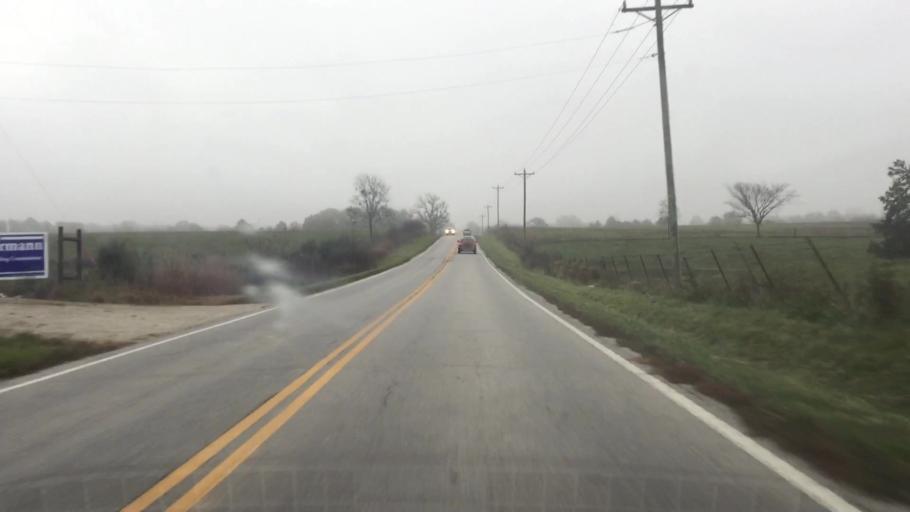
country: US
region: Missouri
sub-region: Callaway County
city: Fulton
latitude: 38.8739
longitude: -92.0551
